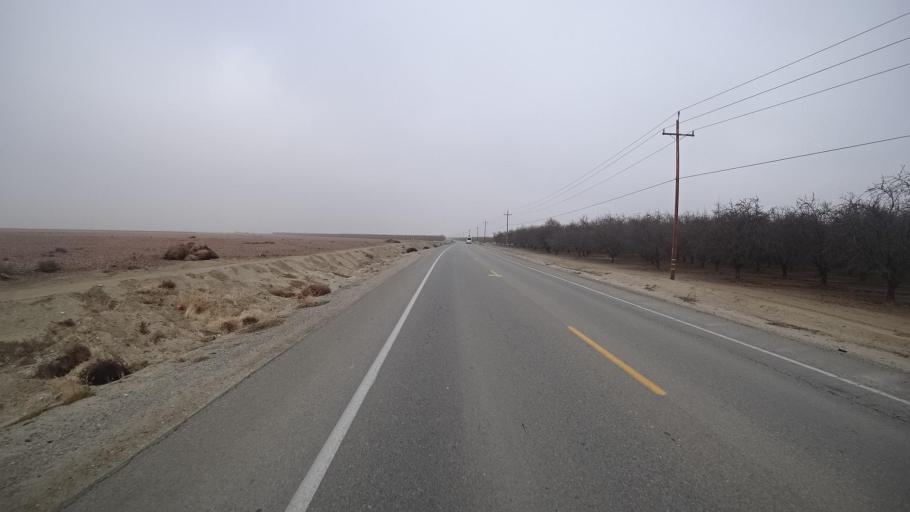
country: US
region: California
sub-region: Kern County
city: Greenfield
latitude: 35.0829
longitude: -119.1204
